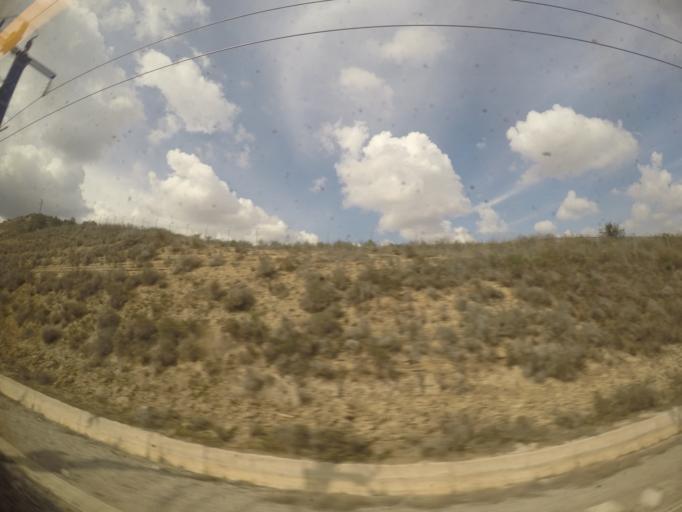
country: ES
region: Catalonia
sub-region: Provincia de Barcelona
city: Sant Llorenc d'Hortons
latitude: 41.4540
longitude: 1.8470
